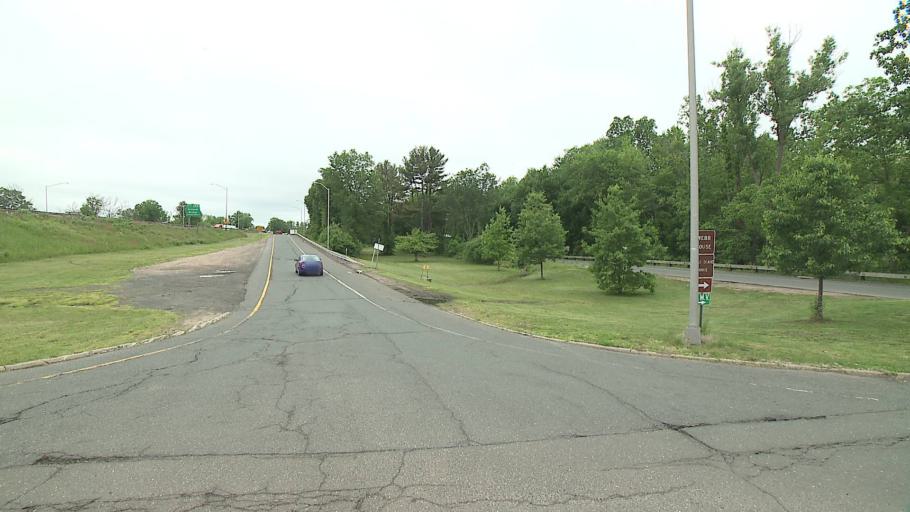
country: US
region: Connecticut
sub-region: Hartford County
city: Wethersfield
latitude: 41.7140
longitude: -72.6488
